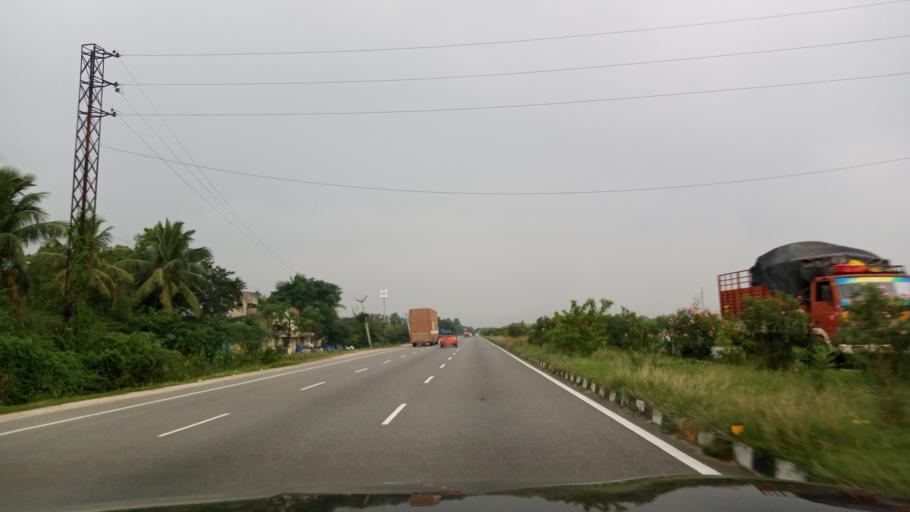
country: IN
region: Tamil Nadu
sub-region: Vellore
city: Arcot
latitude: 12.9123
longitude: 79.3062
